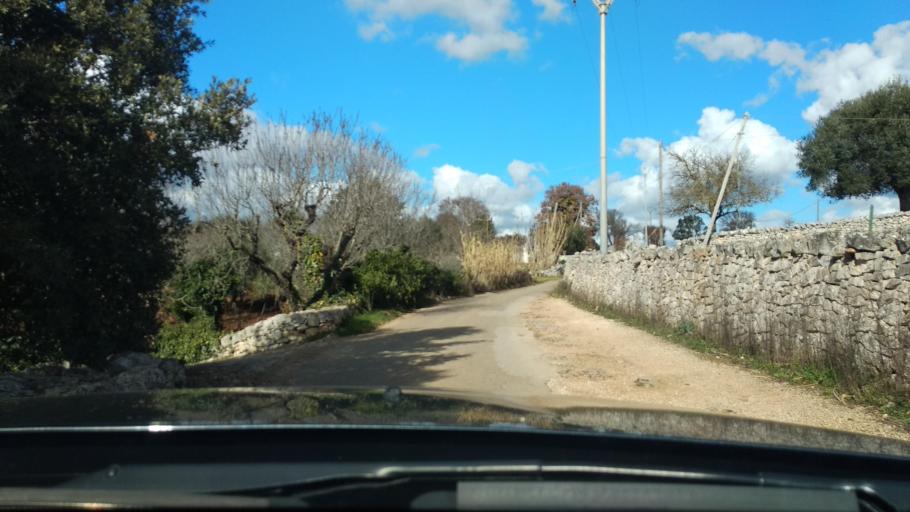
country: IT
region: Apulia
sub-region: Provincia di Brindisi
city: Casalini
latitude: 40.7083
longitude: 17.4533
